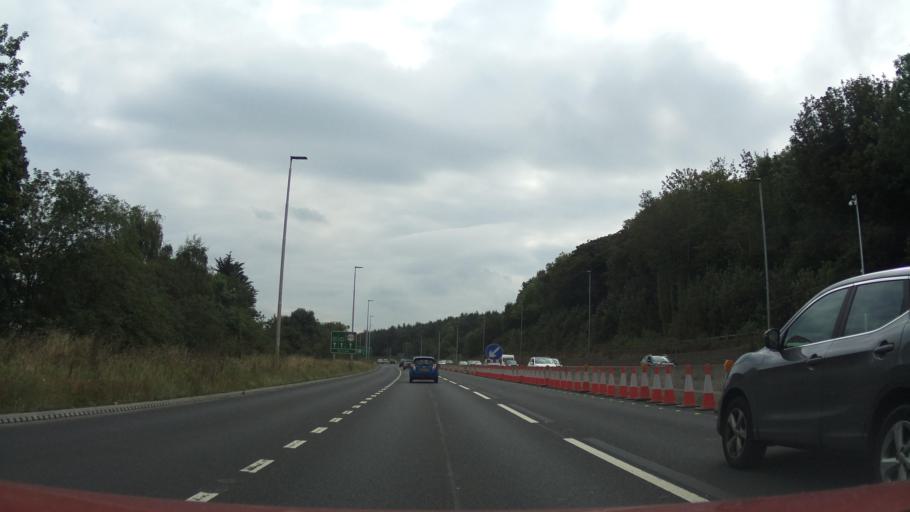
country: GB
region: England
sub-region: Gateshead
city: Lamesley
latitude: 54.9270
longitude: -1.6269
